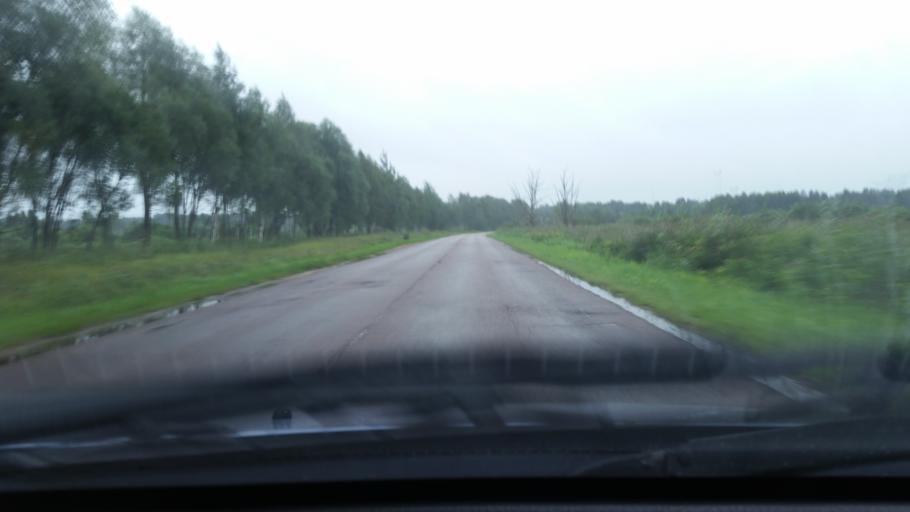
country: LV
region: Riga
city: Bolderaja
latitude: 56.9931
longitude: 24.0309
